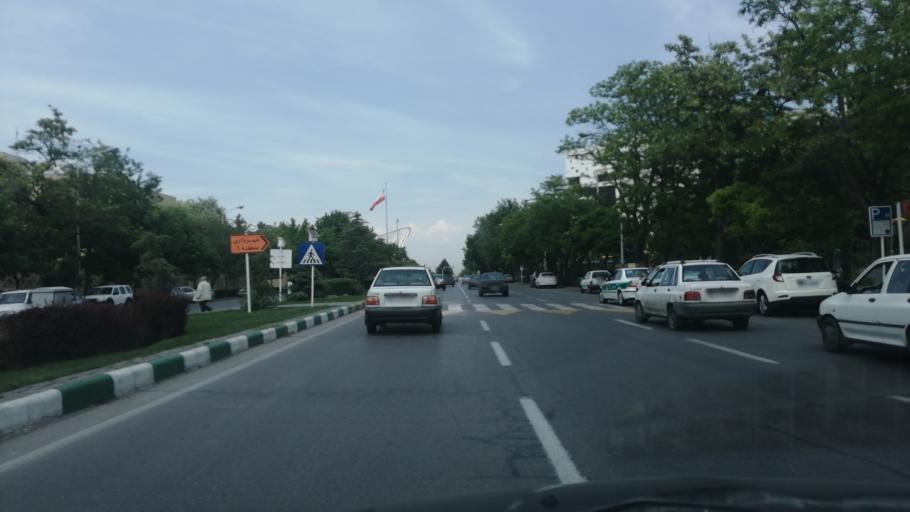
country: IR
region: Razavi Khorasan
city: Mashhad
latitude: 36.3220
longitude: 59.5677
